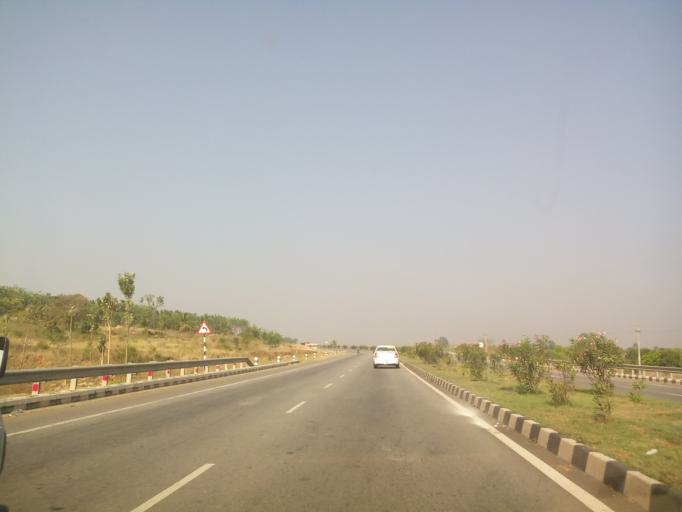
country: IN
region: Karnataka
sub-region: Bangalore Rural
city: Nelamangala
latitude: 13.0660
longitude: 77.3117
